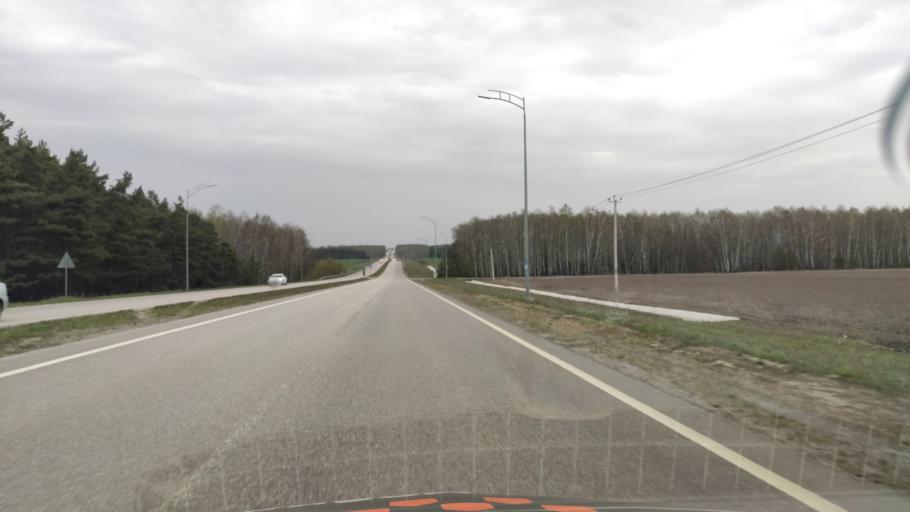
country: RU
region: Belgorod
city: Staryy Oskol
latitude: 51.4004
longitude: 37.8750
